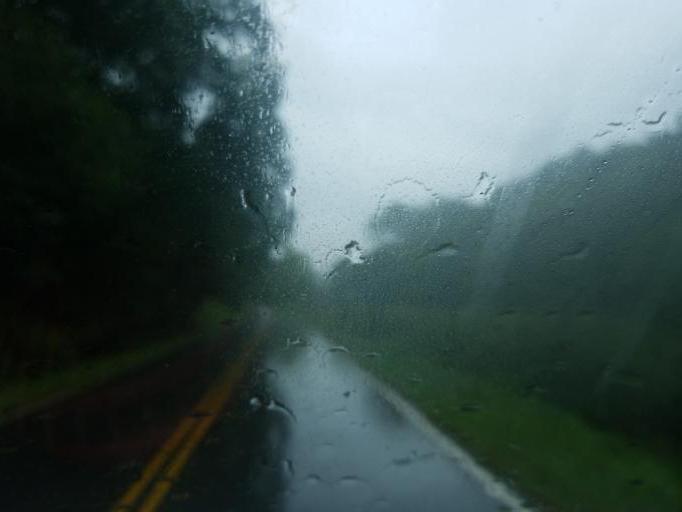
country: US
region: Kentucky
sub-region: Carter County
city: Grayson
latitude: 38.4936
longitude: -82.9938
